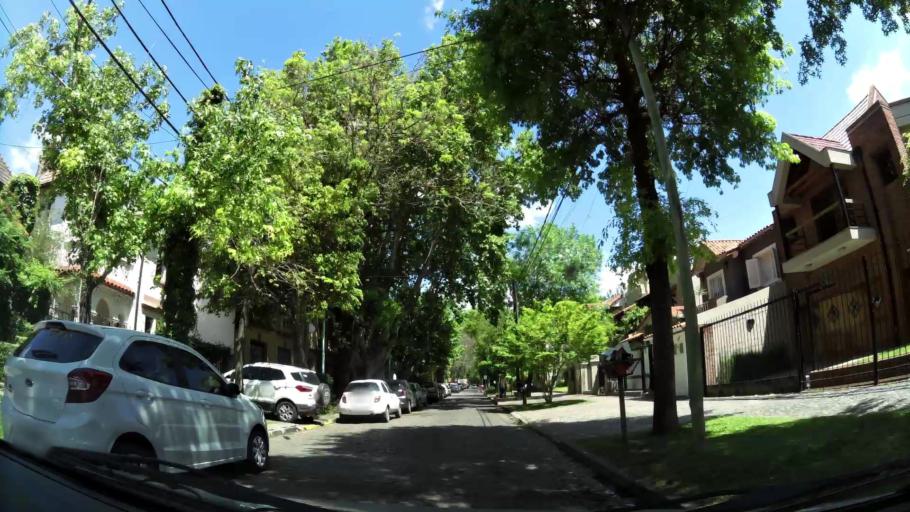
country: AR
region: Buenos Aires
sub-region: Partido de Lomas de Zamora
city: Lomas de Zamora
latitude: -34.7406
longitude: -58.4000
